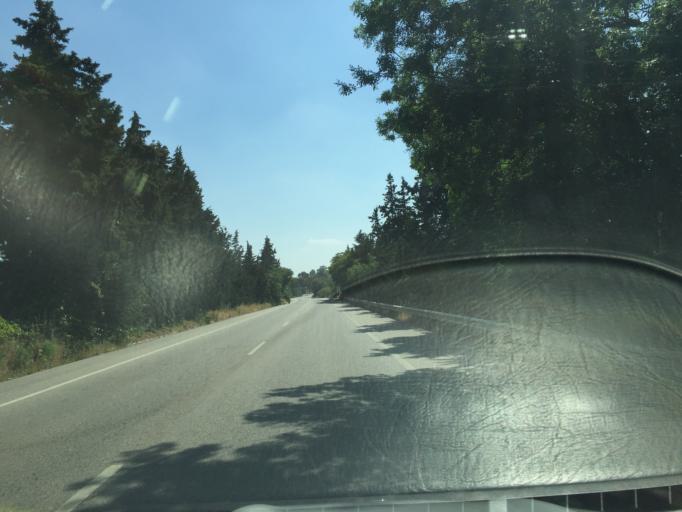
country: PT
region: Santarem
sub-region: Golega
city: Golega
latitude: 39.3833
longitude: -8.4516
